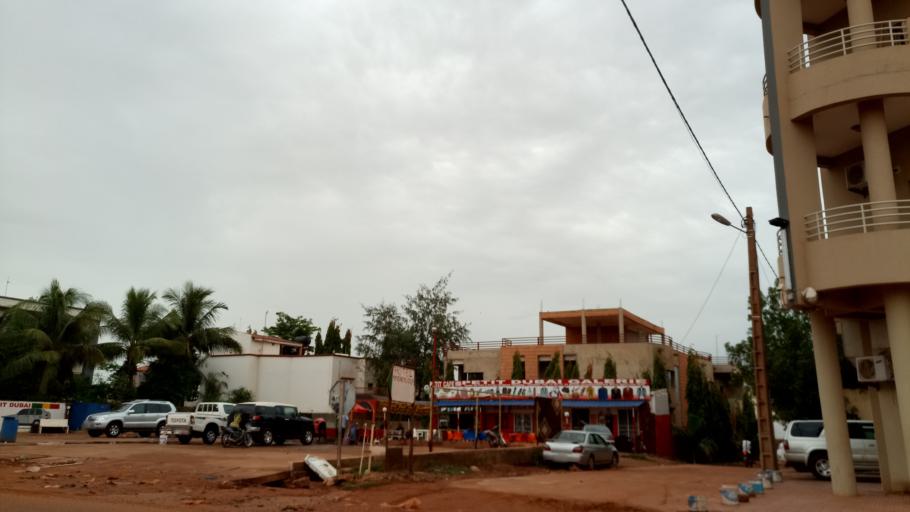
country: ML
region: Bamako
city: Bamako
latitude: 12.5801
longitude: -8.0065
